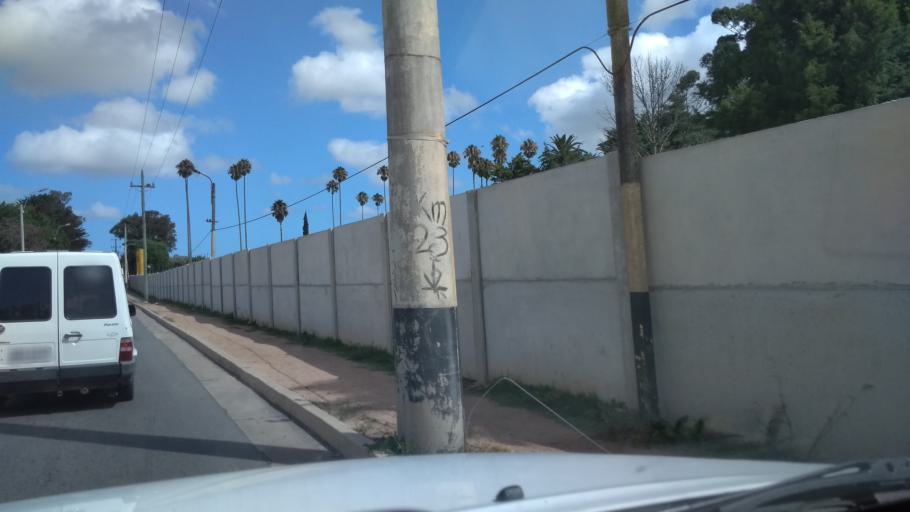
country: UY
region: Canelones
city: Joaquin Suarez
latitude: -34.7724
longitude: -56.0196
